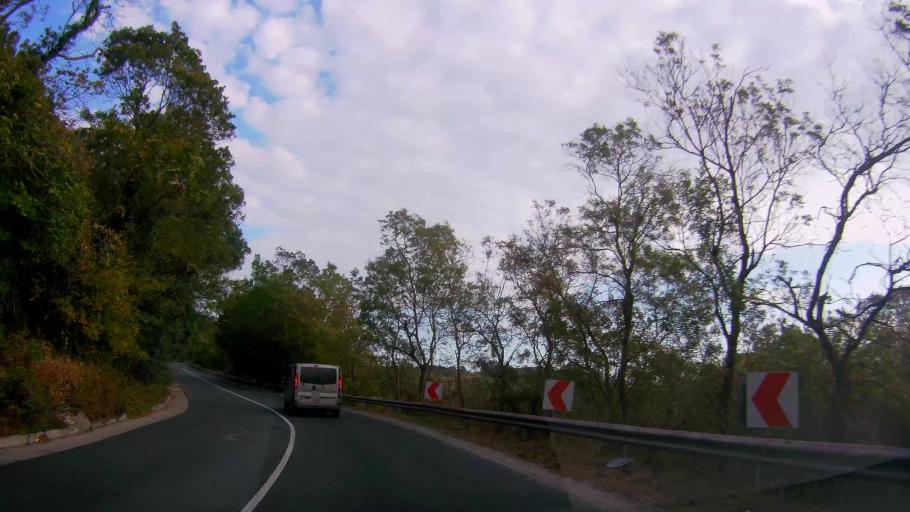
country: BG
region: Burgas
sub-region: Obshtina Primorsko
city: Primorsko
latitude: 42.3182
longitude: 27.7318
